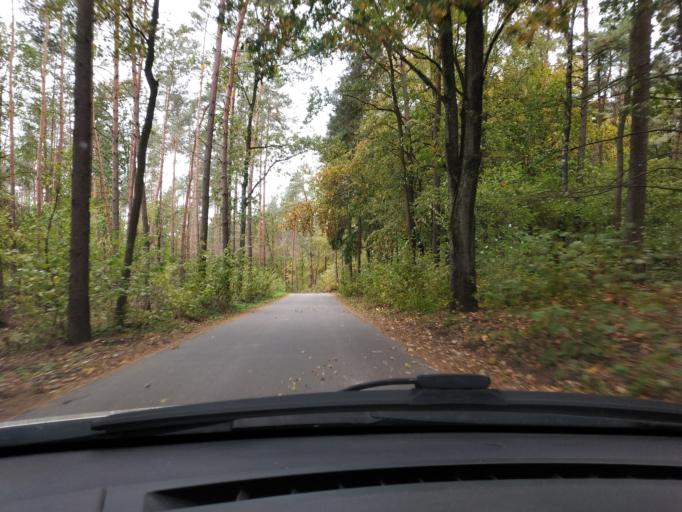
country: PL
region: Warmian-Masurian Voivodeship
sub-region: Powiat nowomiejski
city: Biskupiec
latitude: 53.4505
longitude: 19.3068
